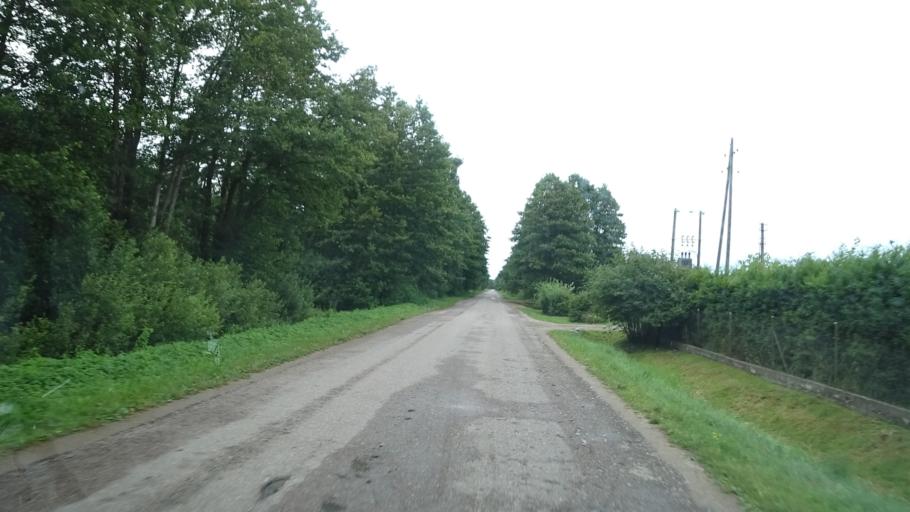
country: LV
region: Liepaja
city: Vec-Liepaja
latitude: 56.6128
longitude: 21.0391
